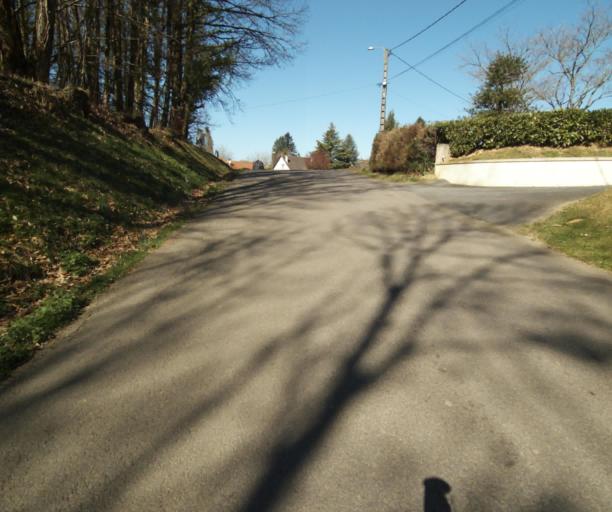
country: FR
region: Limousin
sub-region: Departement de la Correze
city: Saint-Clement
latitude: 45.3456
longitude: 1.6392
